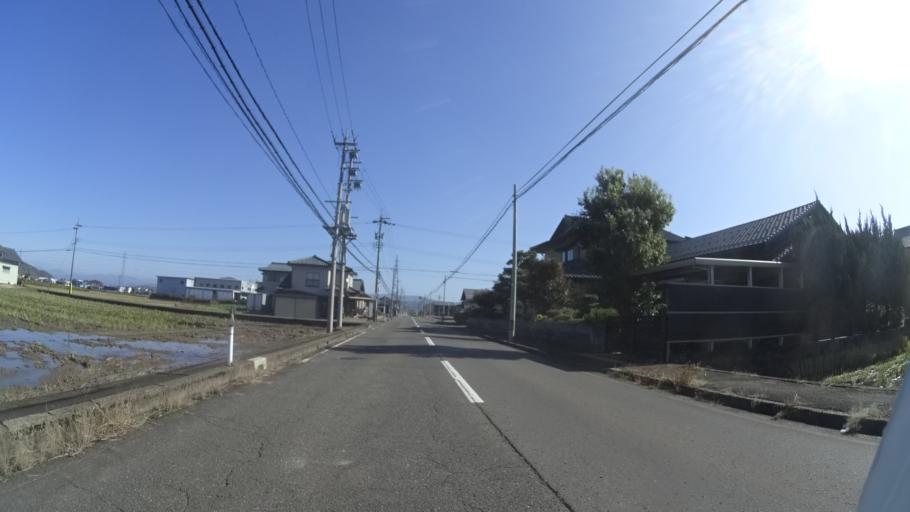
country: JP
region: Fukui
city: Sabae
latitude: 35.9640
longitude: 136.1590
